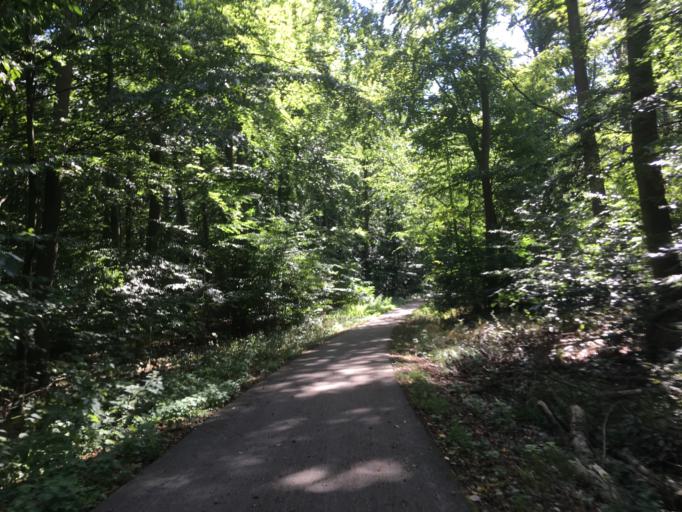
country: DE
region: Brandenburg
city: Gerswalde
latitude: 53.1143
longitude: 13.8595
